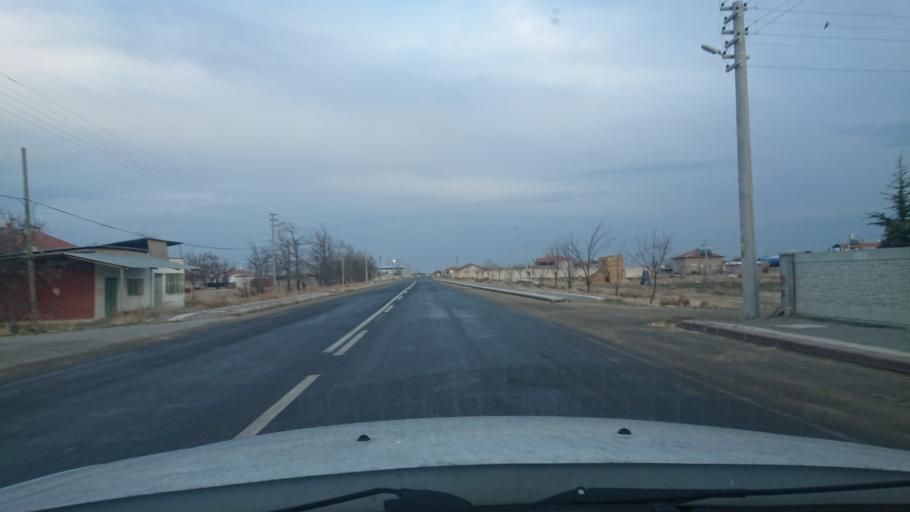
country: TR
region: Aksaray
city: Yesilova
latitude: 38.2925
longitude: 33.7600
